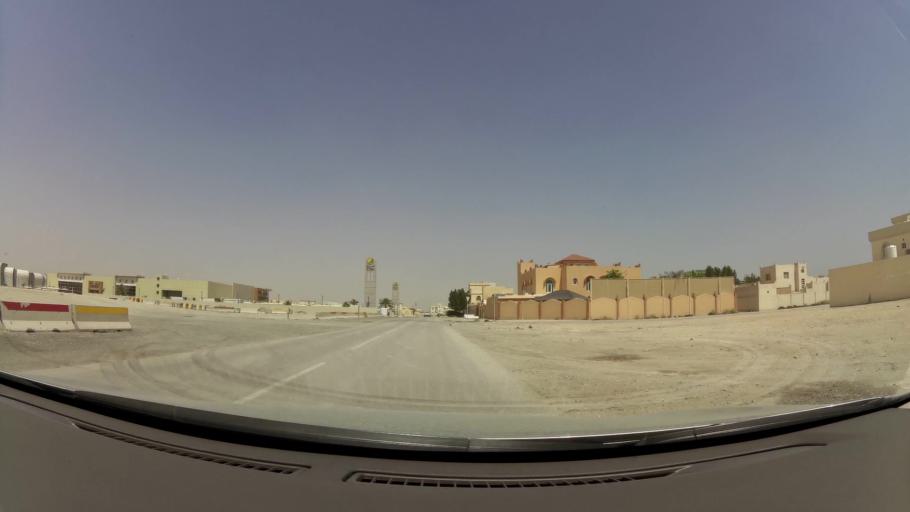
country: QA
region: Baladiyat Umm Salal
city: Umm Salal Muhammad
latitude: 25.3680
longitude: 51.4757
